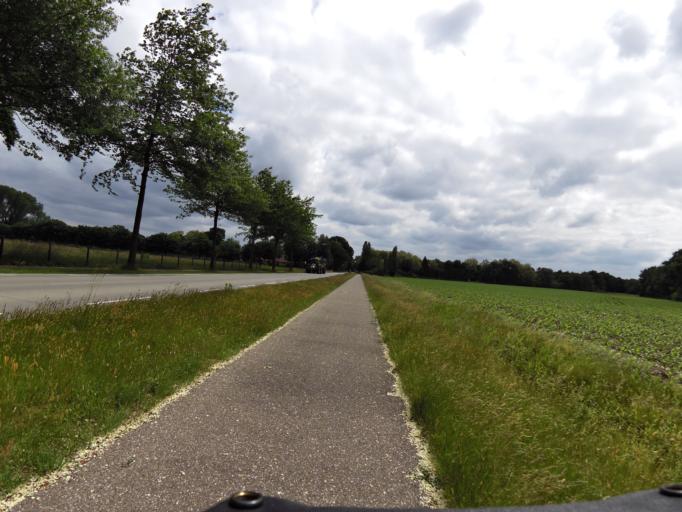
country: NL
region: North Brabant
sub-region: Gemeente Baarle-Nassau
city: Baarle-Nassau
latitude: 51.4519
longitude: 4.8842
